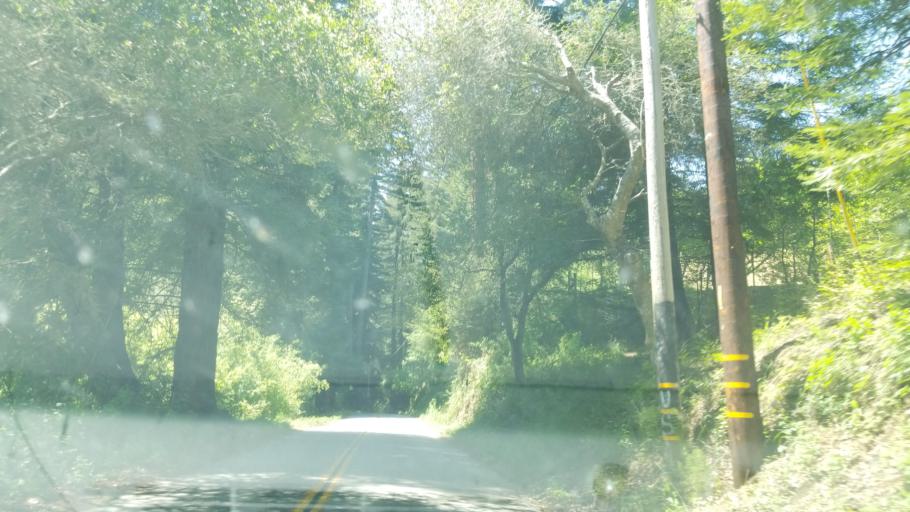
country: US
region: California
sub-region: Santa Cruz County
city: Corralitos
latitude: 37.0196
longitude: -121.7599
